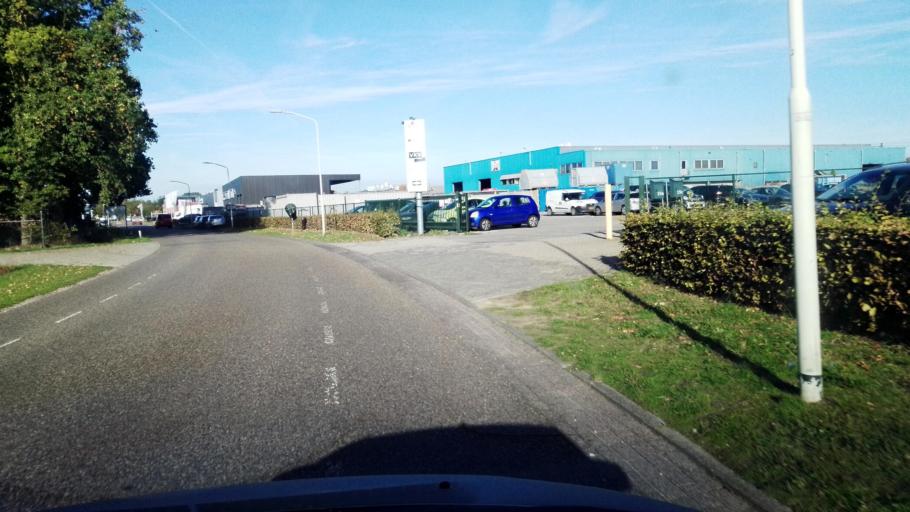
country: NL
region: North Brabant
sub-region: Gemeente Asten
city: Asten
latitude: 51.4568
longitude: 5.7778
